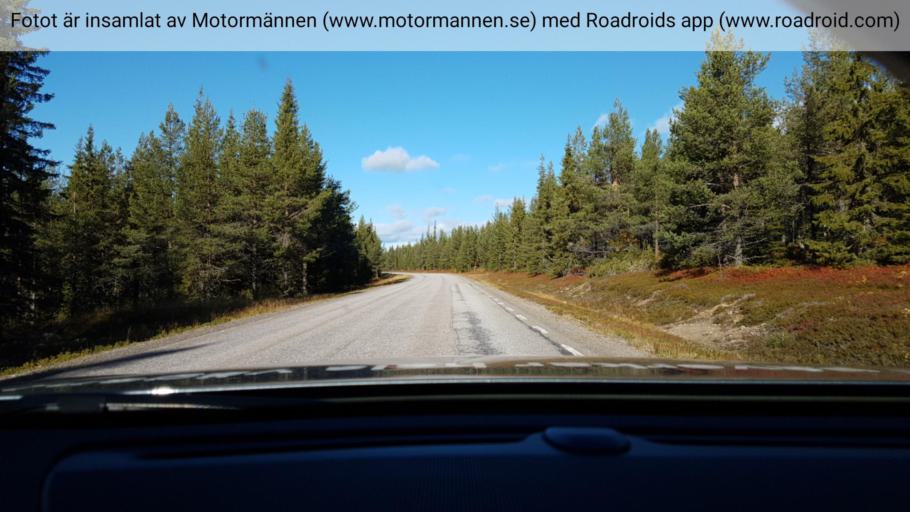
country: SE
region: Norrbotten
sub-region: Arjeplogs Kommun
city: Arjeplog
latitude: 65.8080
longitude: 18.4604
